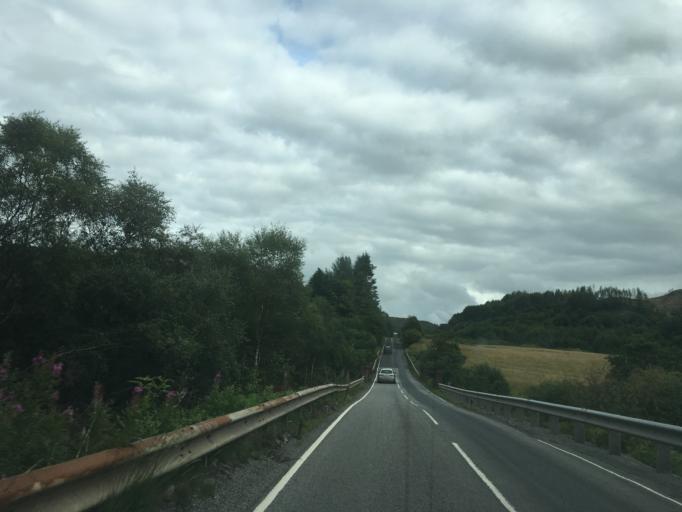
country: GB
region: Scotland
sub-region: Argyll and Bute
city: Oban
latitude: 56.3207
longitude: -5.4949
